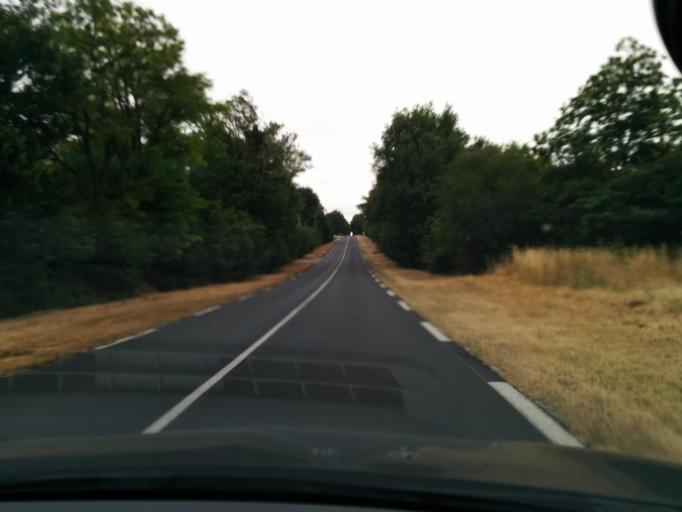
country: FR
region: Ile-de-France
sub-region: Departement de l'Essonne
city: Pussay
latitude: 48.3611
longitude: 1.9830
